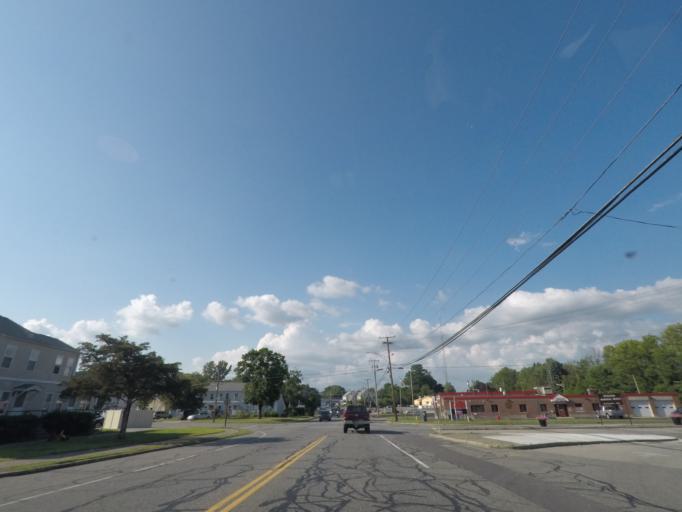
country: US
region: Massachusetts
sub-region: Worcester County
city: Webster
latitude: 42.0540
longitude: -71.8631
